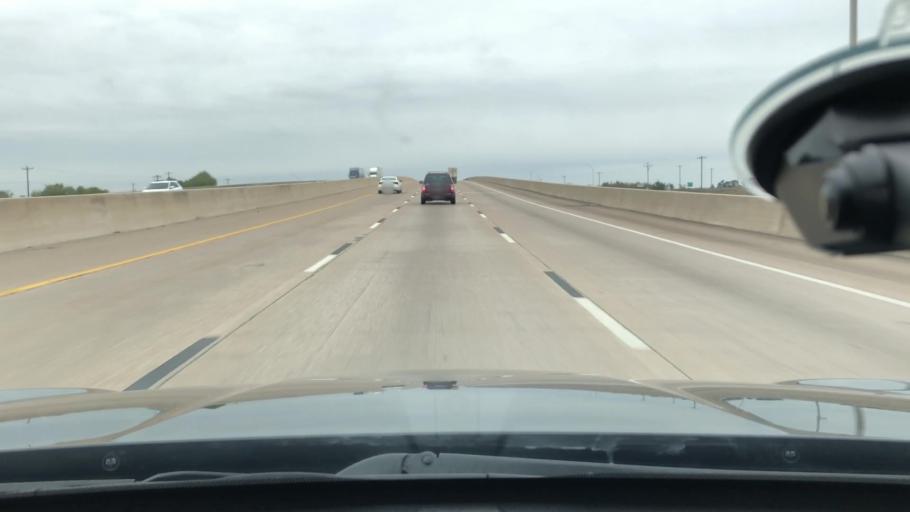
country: US
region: Texas
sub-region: Hill County
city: Hillsboro
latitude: 31.9356
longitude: -97.1060
